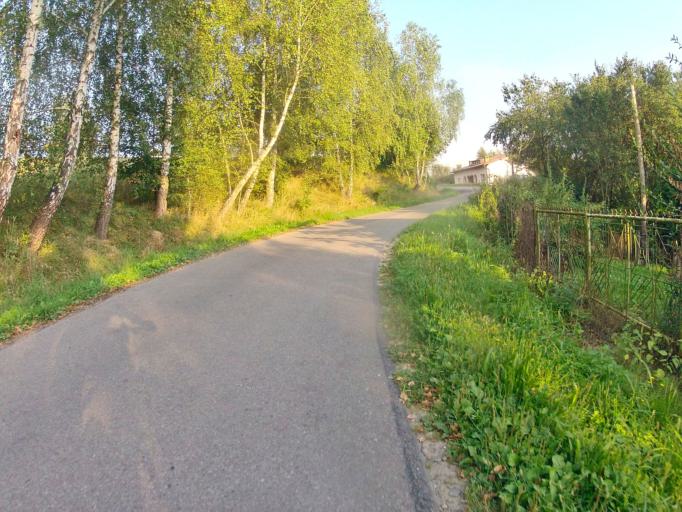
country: PL
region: Subcarpathian Voivodeship
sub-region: Powiat jasielski
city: Brzyska
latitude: 49.7891
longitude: 21.3737
